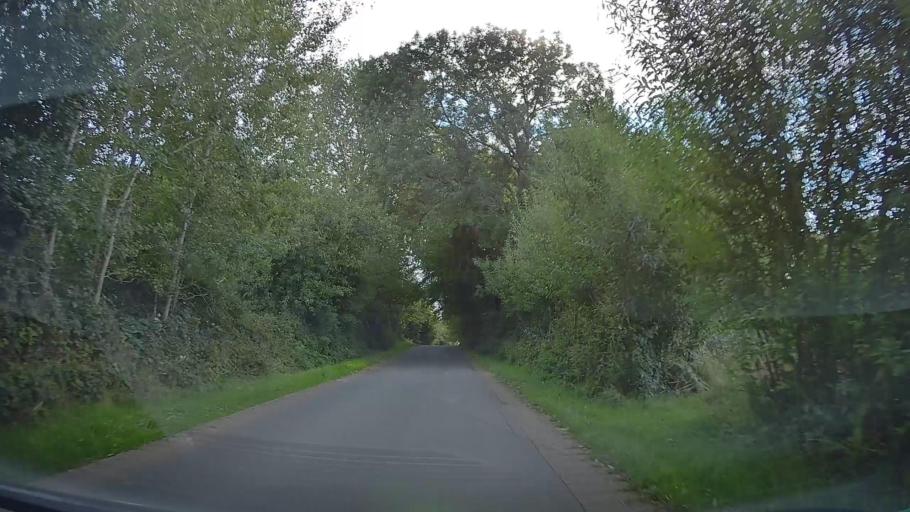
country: DE
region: Schleswig-Holstein
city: Ringsberg
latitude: 54.8260
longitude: 9.6049
